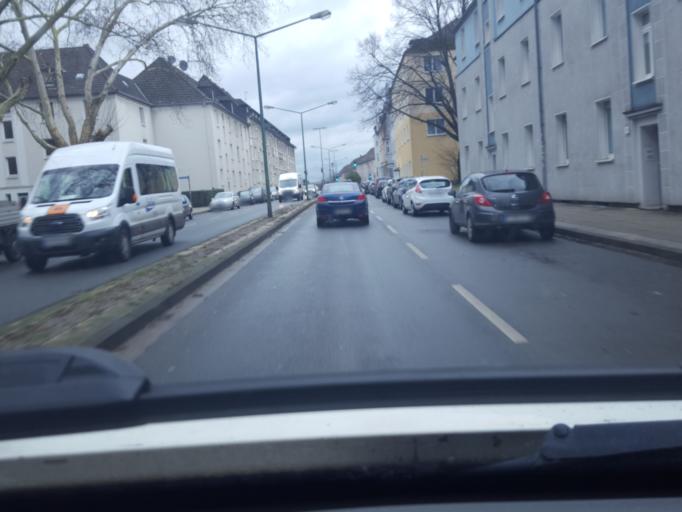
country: DE
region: North Rhine-Westphalia
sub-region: Regierungsbezirk Dusseldorf
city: Essen
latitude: 51.4512
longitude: 6.9640
